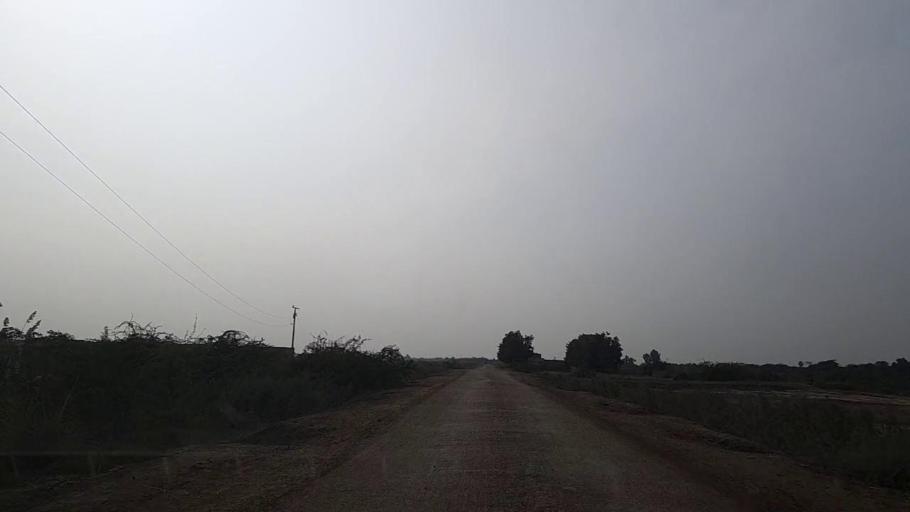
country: PK
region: Sindh
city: Mirpur Sakro
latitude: 24.6439
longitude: 67.6086
